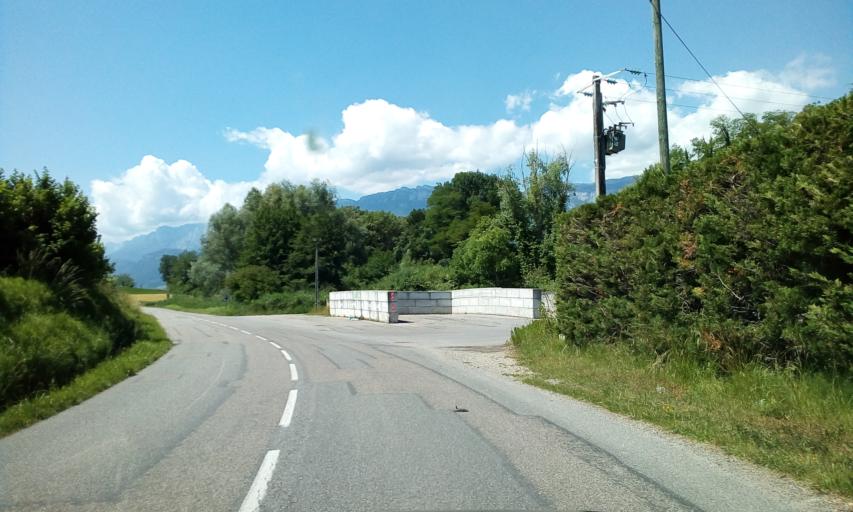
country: FR
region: Rhone-Alpes
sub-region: Departement de la Savoie
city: Montmelian
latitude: 45.4756
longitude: 6.0516
